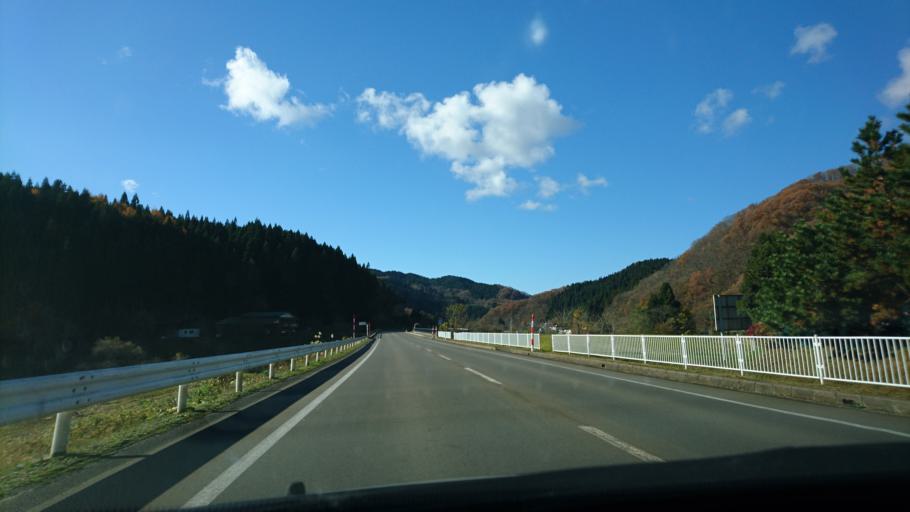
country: JP
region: Akita
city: Omagari
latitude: 39.3158
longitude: 140.2111
